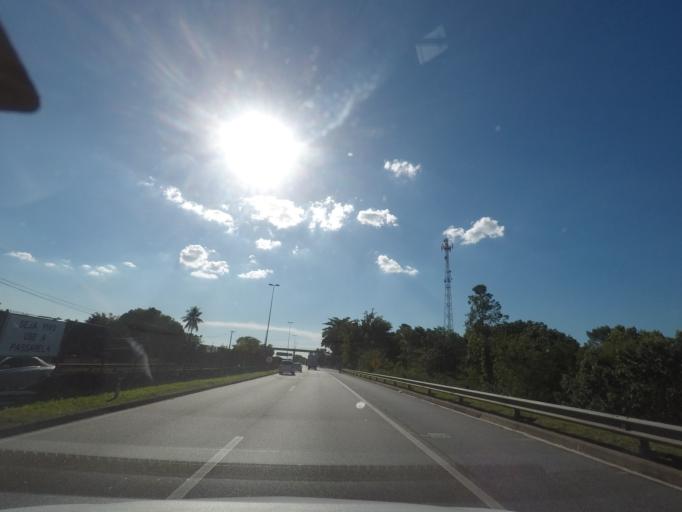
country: BR
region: Rio de Janeiro
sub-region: Petropolis
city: Petropolis
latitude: -22.6463
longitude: -43.2049
